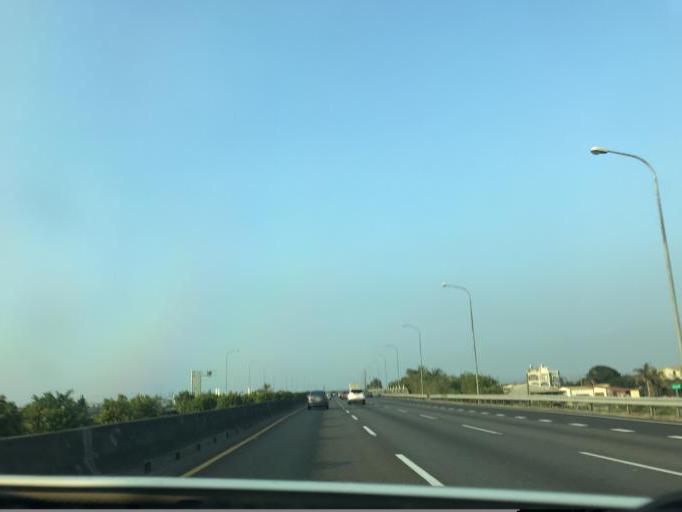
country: TW
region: Taiwan
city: Xinying
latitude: 23.2084
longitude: 120.2371
